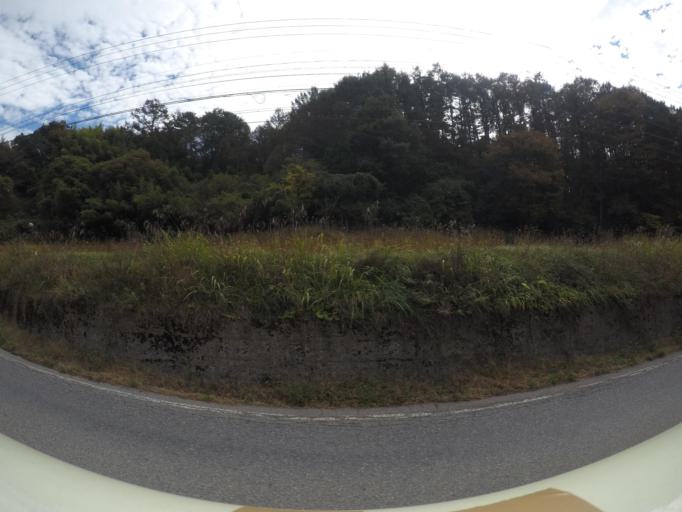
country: JP
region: Nagano
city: Chino
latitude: 35.8711
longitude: 138.0926
